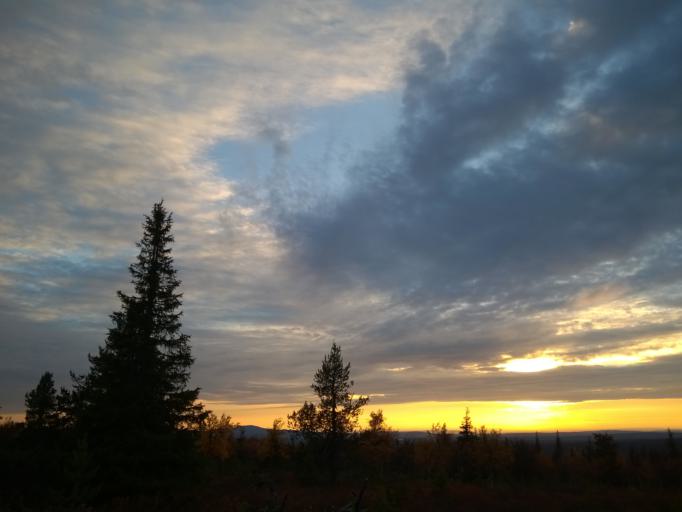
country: FI
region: Lapland
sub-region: Tunturi-Lappi
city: Muonio
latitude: 67.9821
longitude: 24.1089
